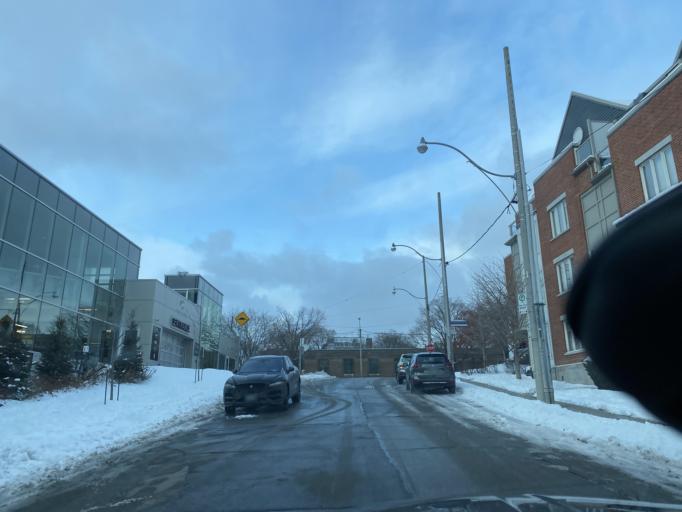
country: CA
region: Ontario
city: Toronto
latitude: 43.6613
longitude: -79.3537
